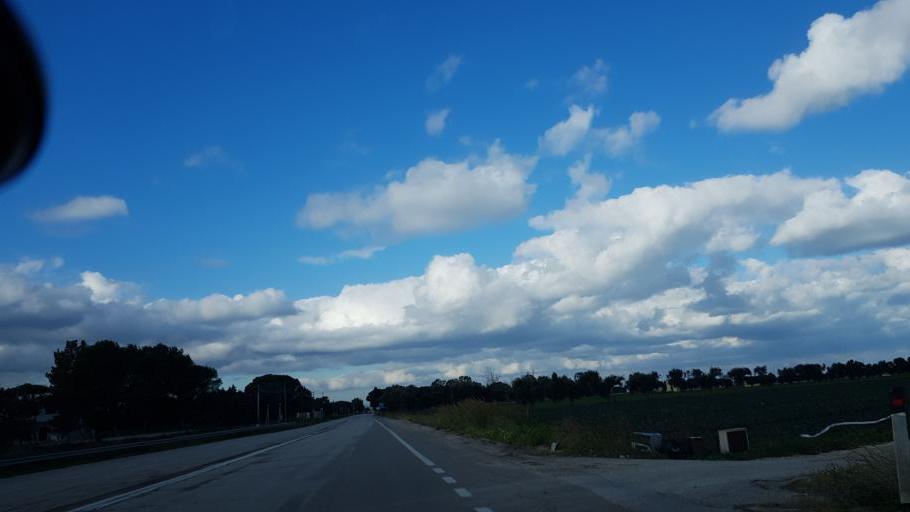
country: IT
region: Apulia
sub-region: Provincia di Brindisi
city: Brindisi
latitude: 40.6455
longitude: 17.9076
